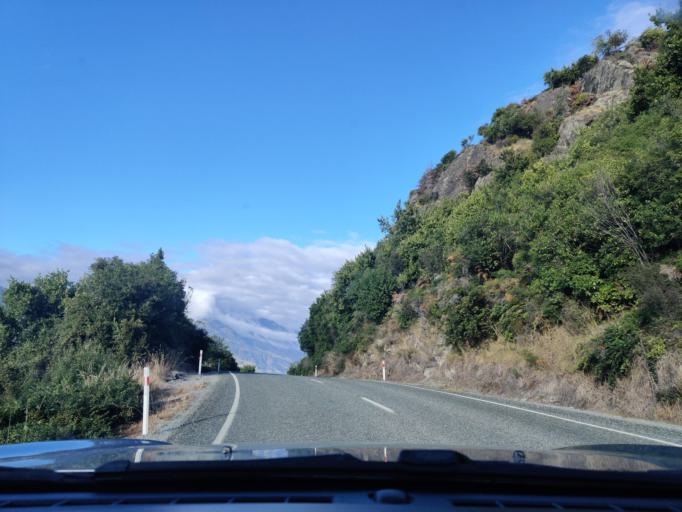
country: NZ
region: Otago
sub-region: Queenstown-Lakes District
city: Queenstown
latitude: -45.0541
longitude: 168.6156
